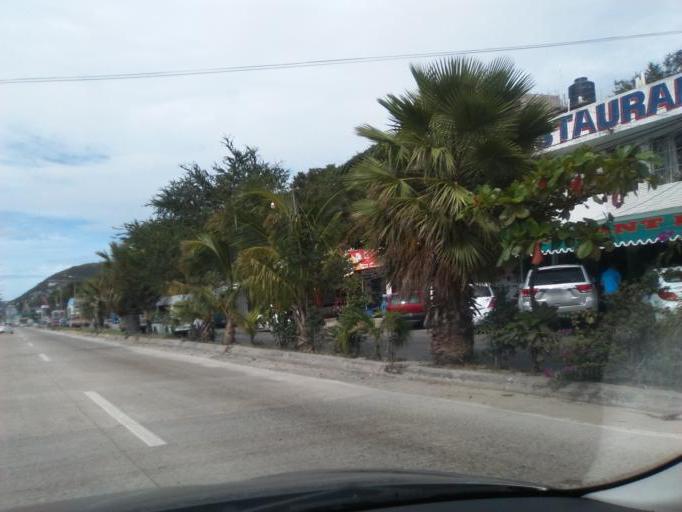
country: MX
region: Guerrero
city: Chilpancingo de los Bravos
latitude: 17.5711
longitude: -99.5124
